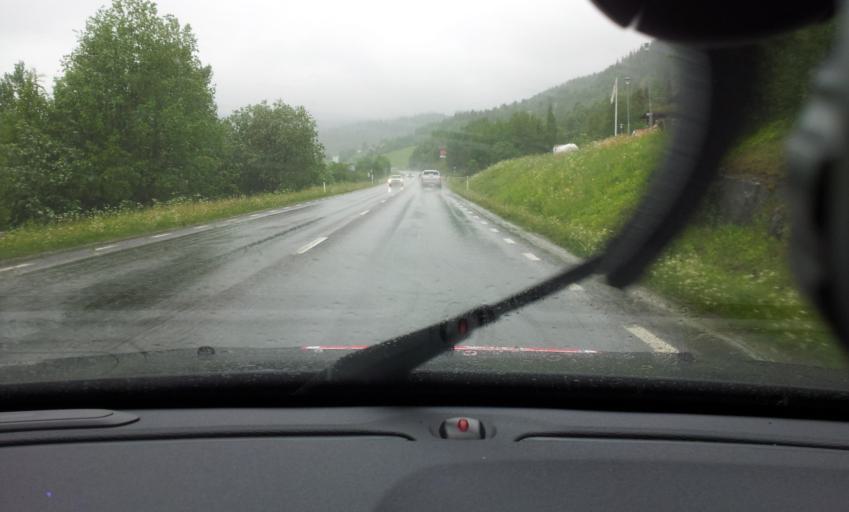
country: SE
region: Jaemtland
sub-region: Are Kommun
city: Are
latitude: 63.3724
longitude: 13.1623
